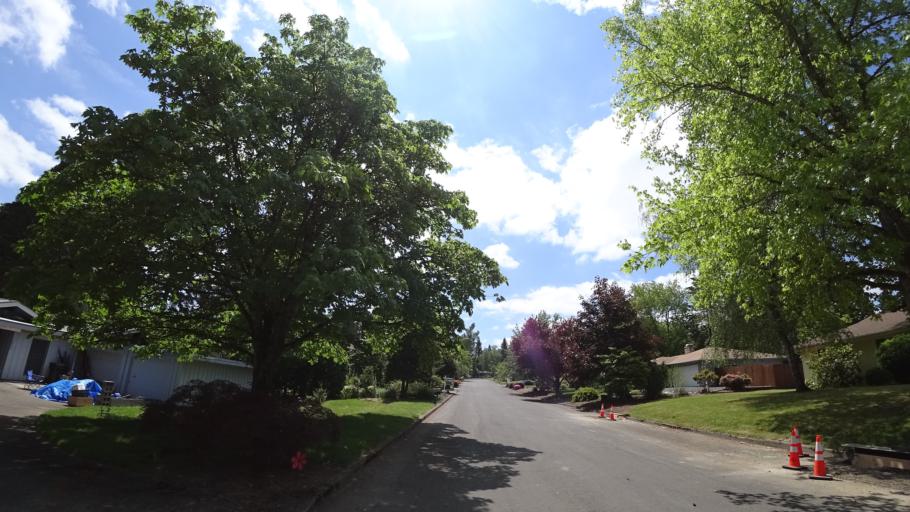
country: US
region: Oregon
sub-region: Washington County
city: Tigard
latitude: 45.4334
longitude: -122.7958
